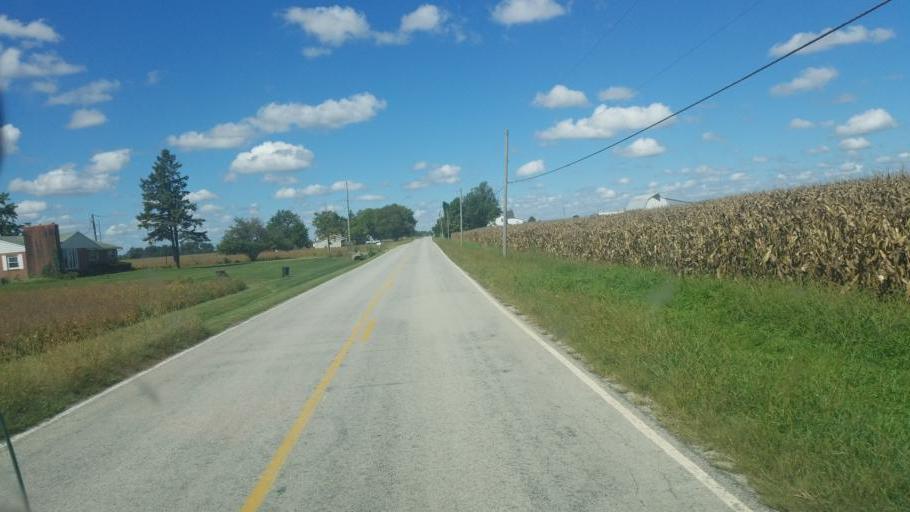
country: US
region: Ohio
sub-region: Madison County
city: West Jefferson
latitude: 39.9953
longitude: -83.2900
